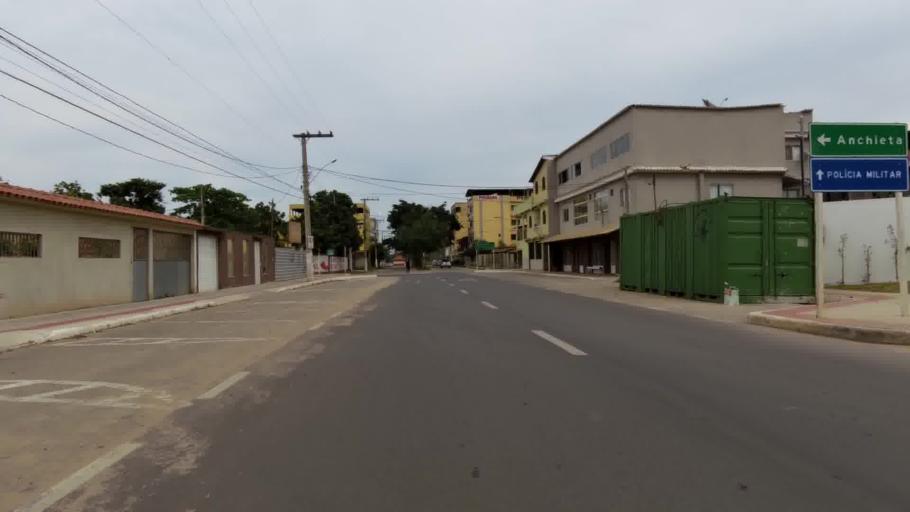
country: BR
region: Espirito Santo
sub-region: Piuma
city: Piuma
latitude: -20.8401
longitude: -40.7292
